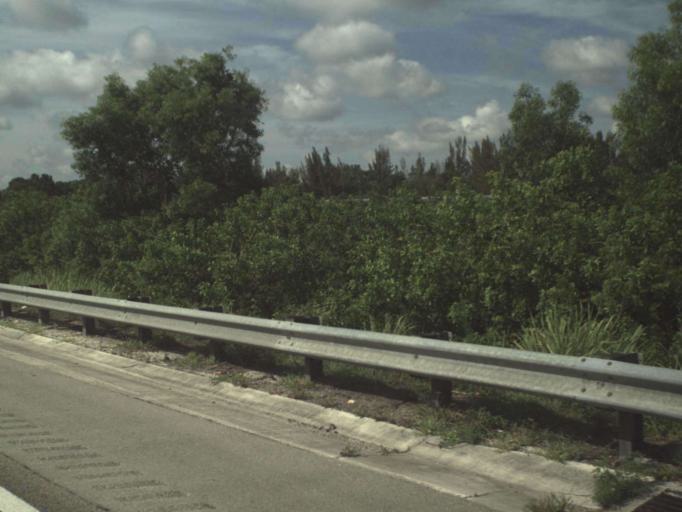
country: US
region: Florida
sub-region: Palm Beach County
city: Limestone Creek
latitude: 26.9323
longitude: -80.1498
